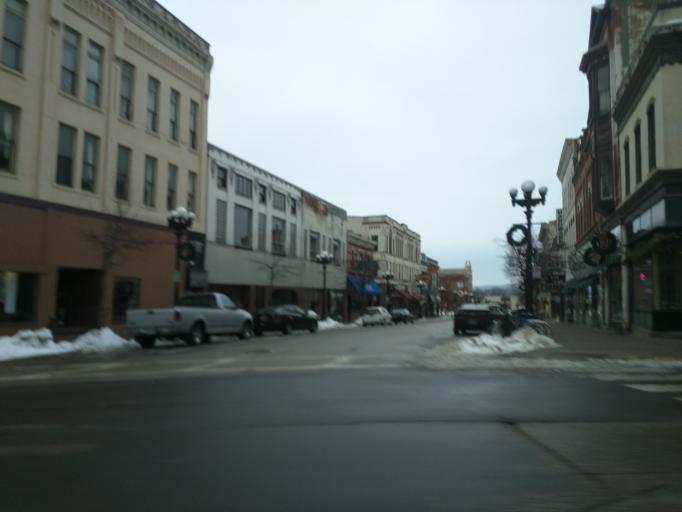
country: US
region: Wisconsin
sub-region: La Crosse County
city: La Crosse
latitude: 43.8115
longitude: -91.2518
